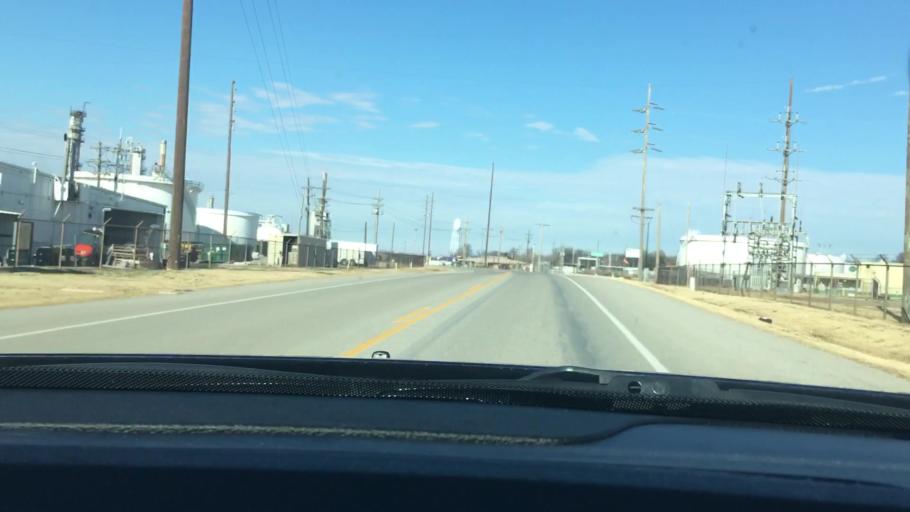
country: US
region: Oklahoma
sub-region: Garvin County
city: Wynnewood
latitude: 34.6312
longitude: -97.1660
